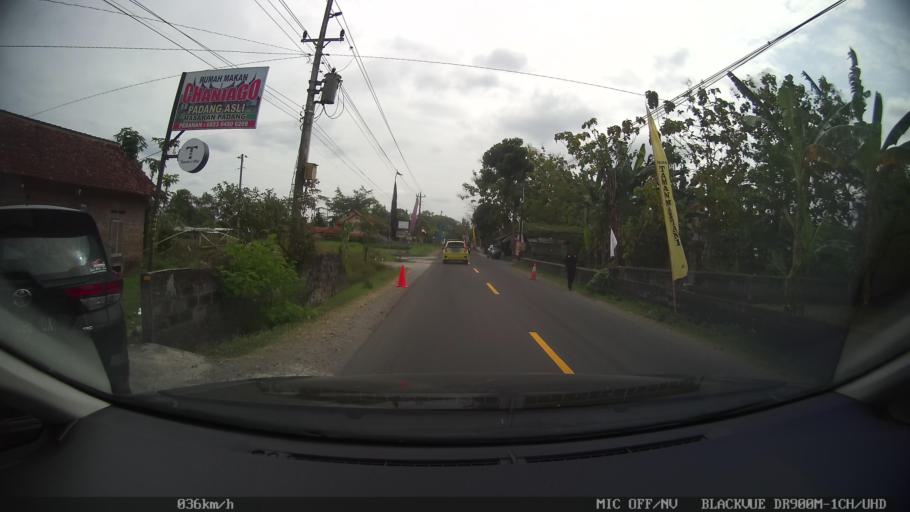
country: ID
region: Central Java
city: Candi Prambanan
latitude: -7.7347
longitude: 110.4741
